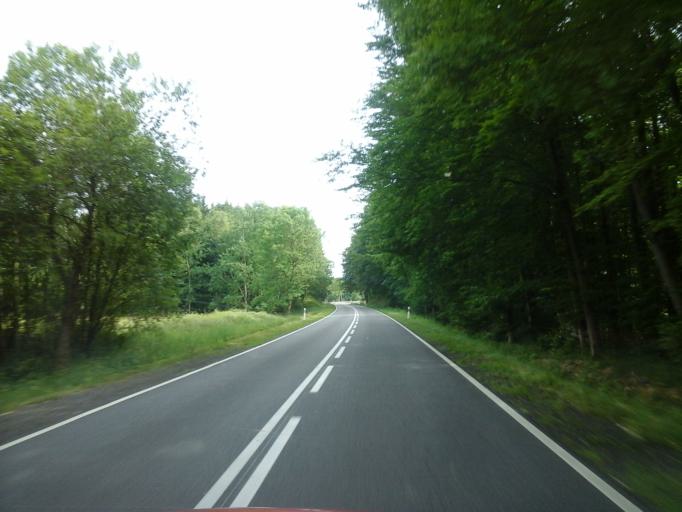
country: PL
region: West Pomeranian Voivodeship
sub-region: Powiat stargardzki
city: Insko
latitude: 53.4833
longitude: 15.5805
